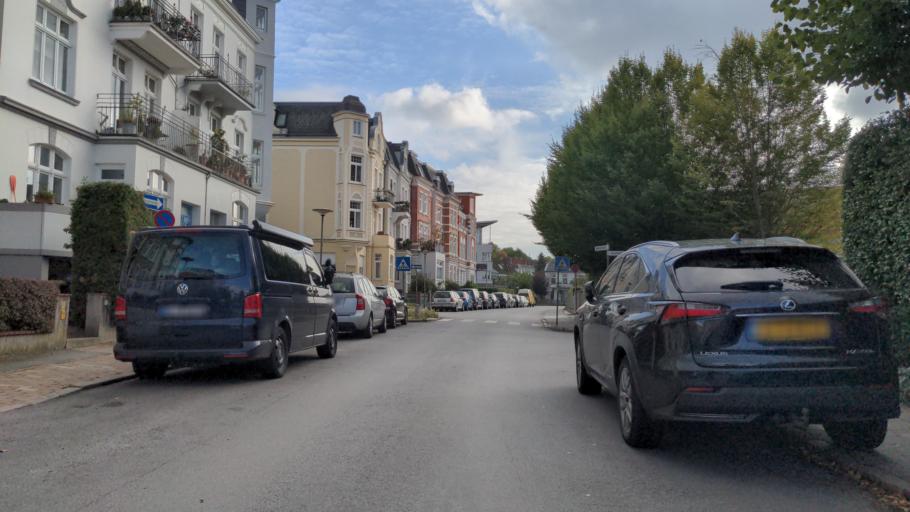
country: DE
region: Schleswig-Holstein
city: Luebeck
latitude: 53.8616
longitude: 10.6982
